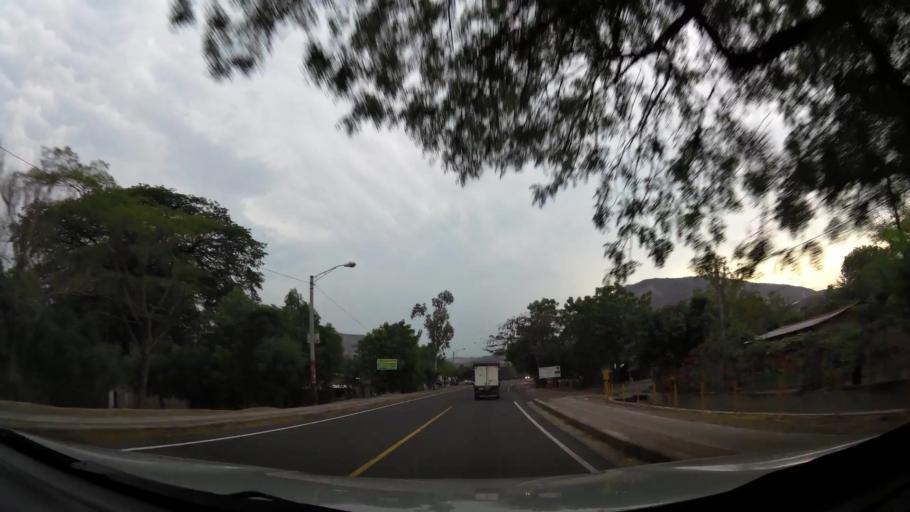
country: NI
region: Matagalpa
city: Ciudad Dario
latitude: 12.9267
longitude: -86.1952
